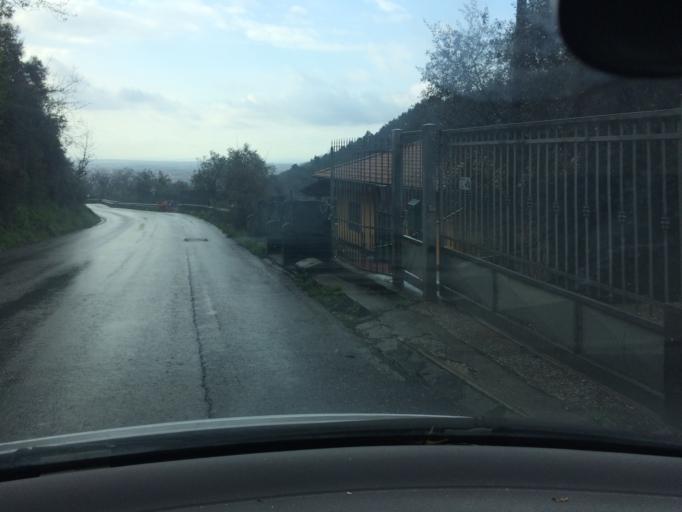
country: IT
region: Tuscany
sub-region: Provincia di Massa-Carrara
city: Massa
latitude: 44.0565
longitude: 10.1229
